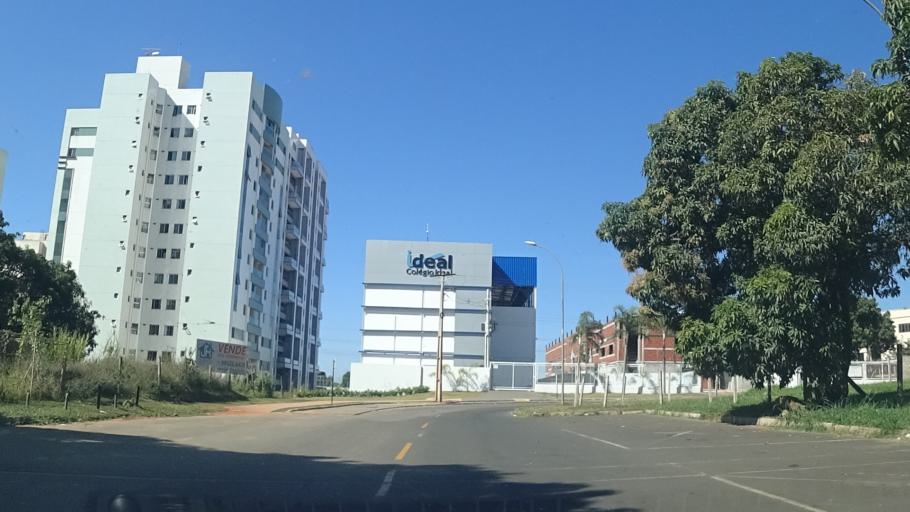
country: BR
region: Federal District
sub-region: Brasilia
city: Brasilia
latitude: -15.8450
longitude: -48.0296
